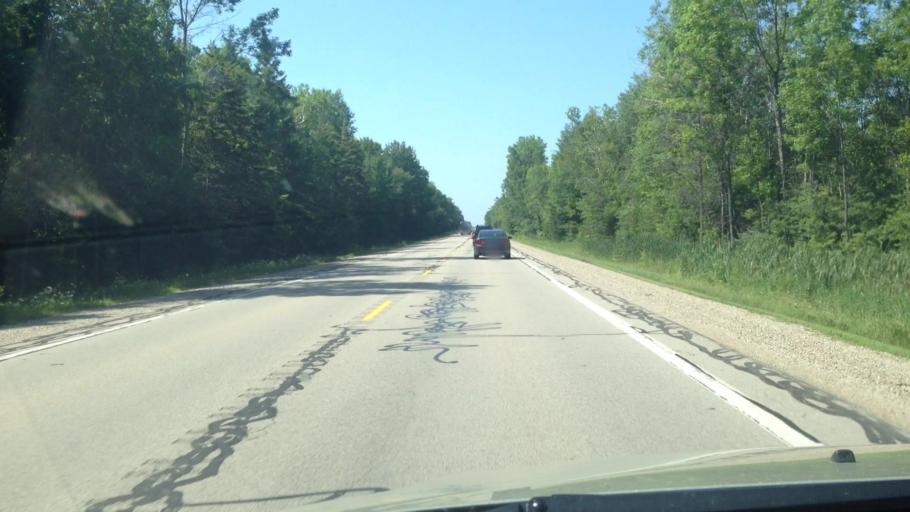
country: US
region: Michigan
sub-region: Menominee County
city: Menominee
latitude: 45.3502
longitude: -87.4064
